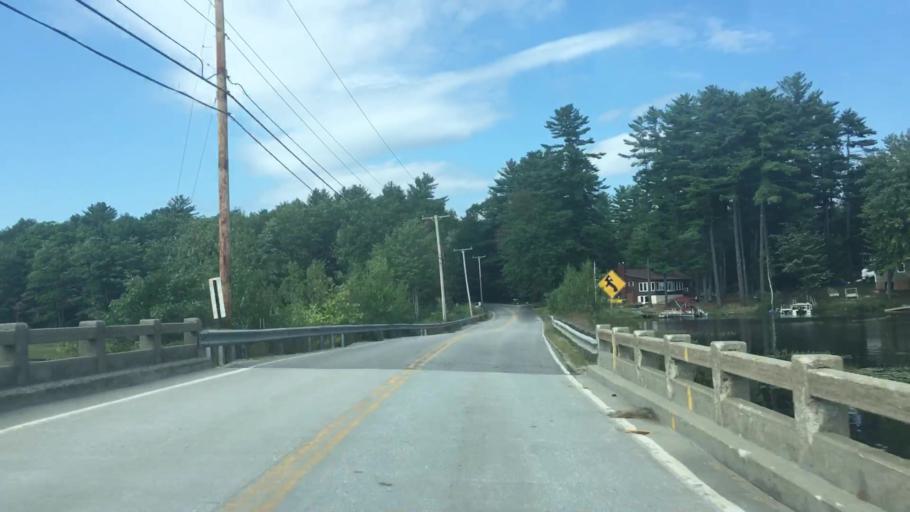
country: US
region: Maine
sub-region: Oxford County
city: Oxford
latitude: 44.1216
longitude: -70.5054
